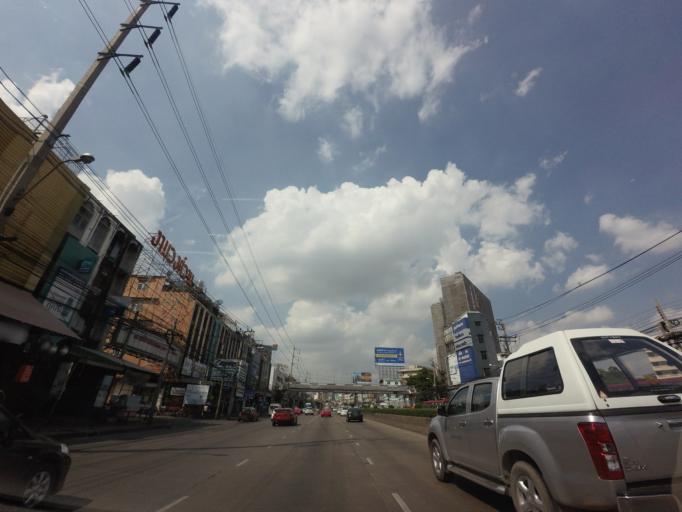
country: TH
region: Bangkok
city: Chatuchak
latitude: 13.8543
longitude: 100.5492
